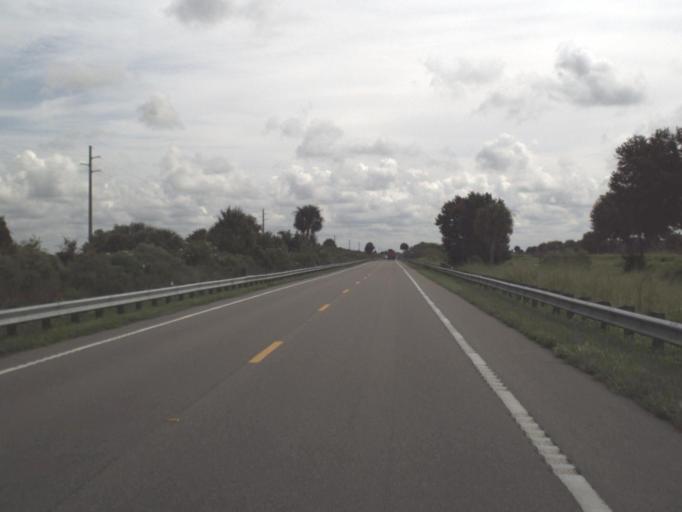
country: US
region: Florida
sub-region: Highlands County
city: Lake Placid
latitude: 27.2095
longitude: -81.1727
